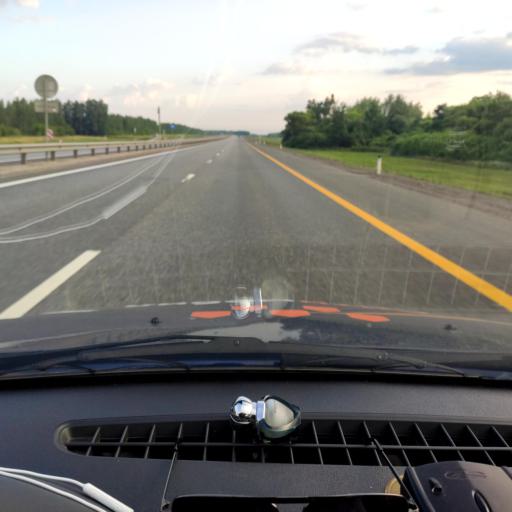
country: RU
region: Lipetsk
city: Zadonsk
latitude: 52.4790
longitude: 38.7625
